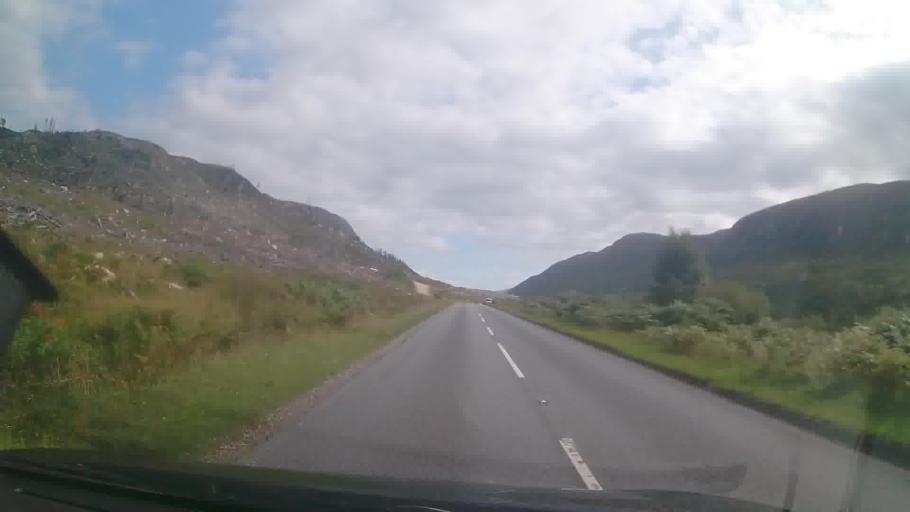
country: GB
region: Scotland
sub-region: Argyll and Bute
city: Oban
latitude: 56.6893
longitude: -5.5029
